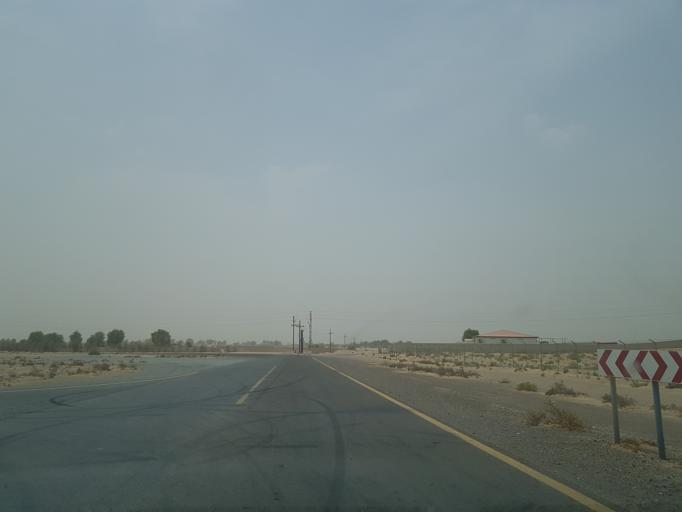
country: AE
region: Dubai
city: Dubai
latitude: 24.9412
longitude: 55.4809
